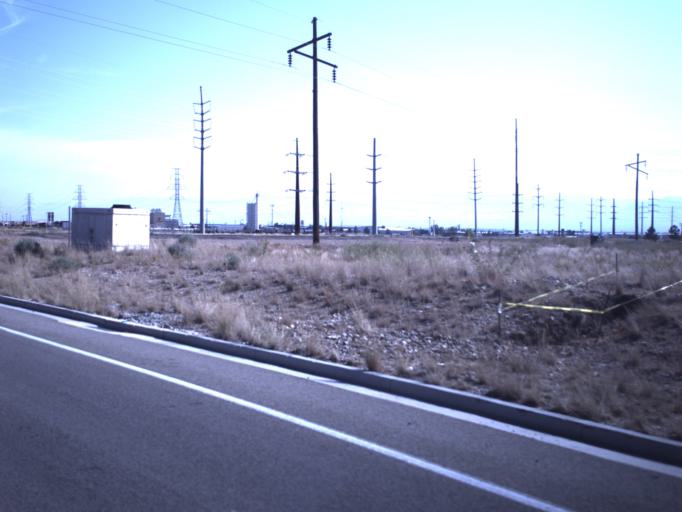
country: US
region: Utah
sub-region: Salt Lake County
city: Herriman
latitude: 40.5669
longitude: -112.0322
